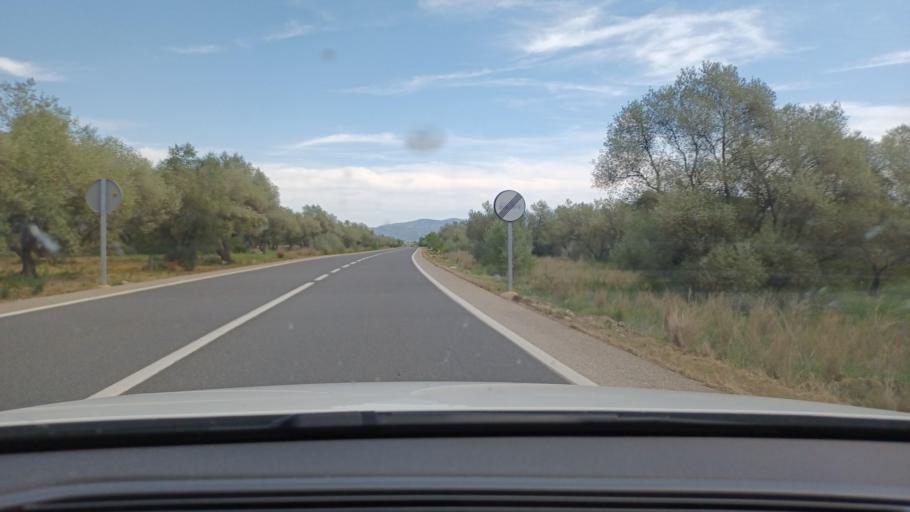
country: ES
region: Catalonia
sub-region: Provincia de Tarragona
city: Mas de Barberans
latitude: 40.6395
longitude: 0.3403
